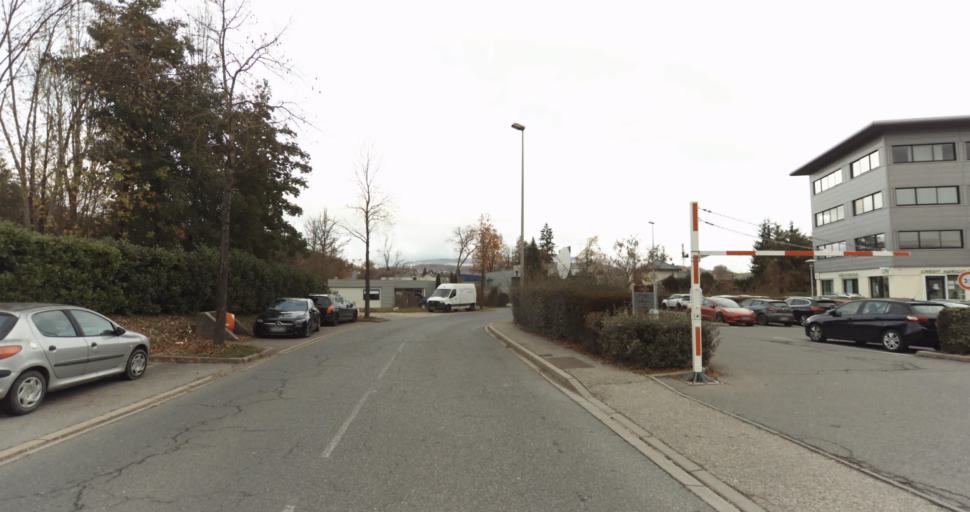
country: FR
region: Rhone-Alpes
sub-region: Departement de la Haute-Savoie
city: Allonzier-la-Caille
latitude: 45.9954
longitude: 6.1232
